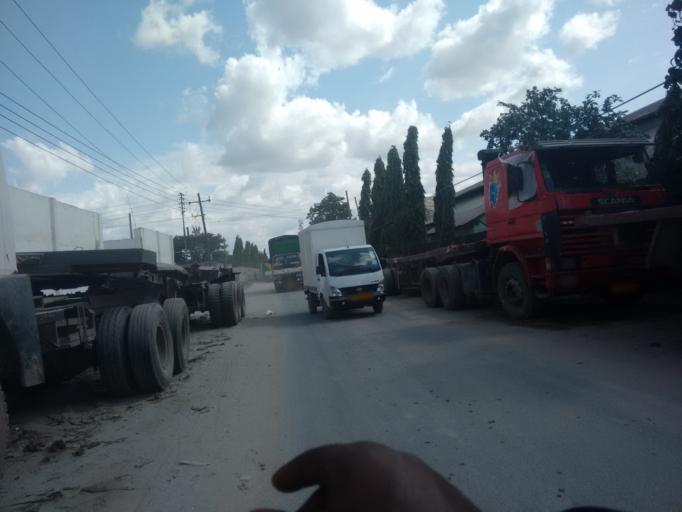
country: TZ
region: Dar es Salaam
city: Dar es Salaam
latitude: -6.8408
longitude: 39.2606
